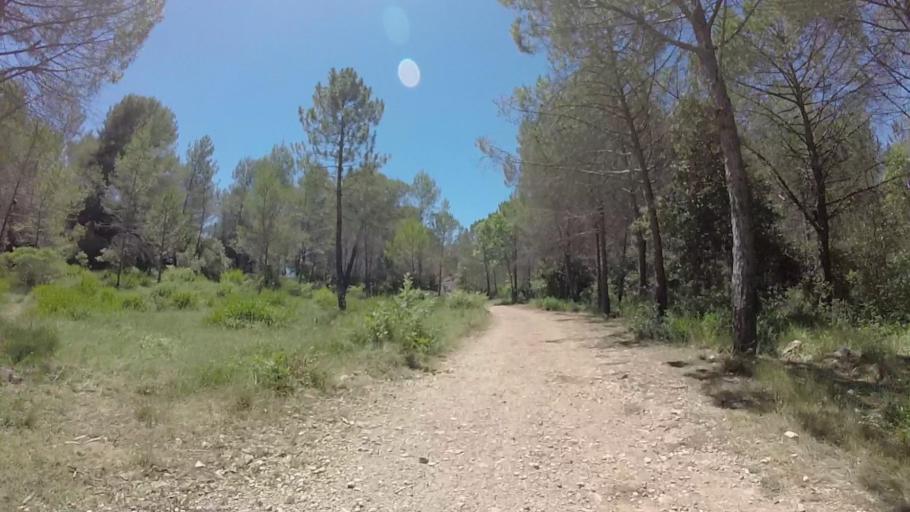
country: FR
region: Provence-Alpes-Cote d'Azur
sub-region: Departement des Alpes-Maritimes
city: Valbonne
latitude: 43.6294
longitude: 7.0362
